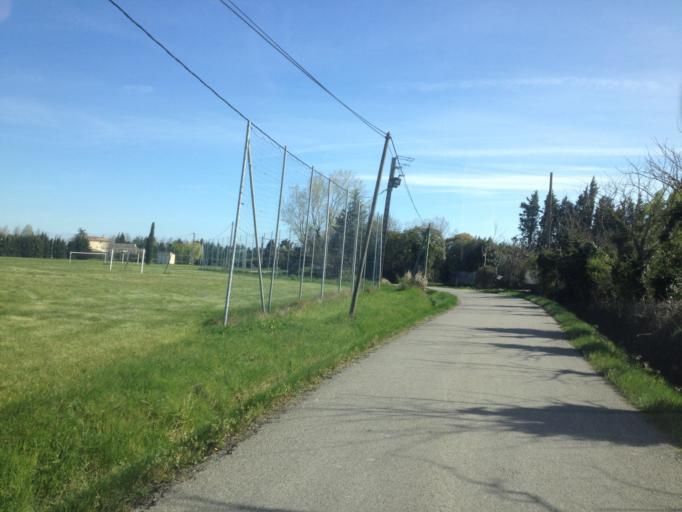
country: FR
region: Provence-Alpes-Cote d'Azur
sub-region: Departement du Vaucluse
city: Caderousse
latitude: 44.1088
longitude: 4.7553
